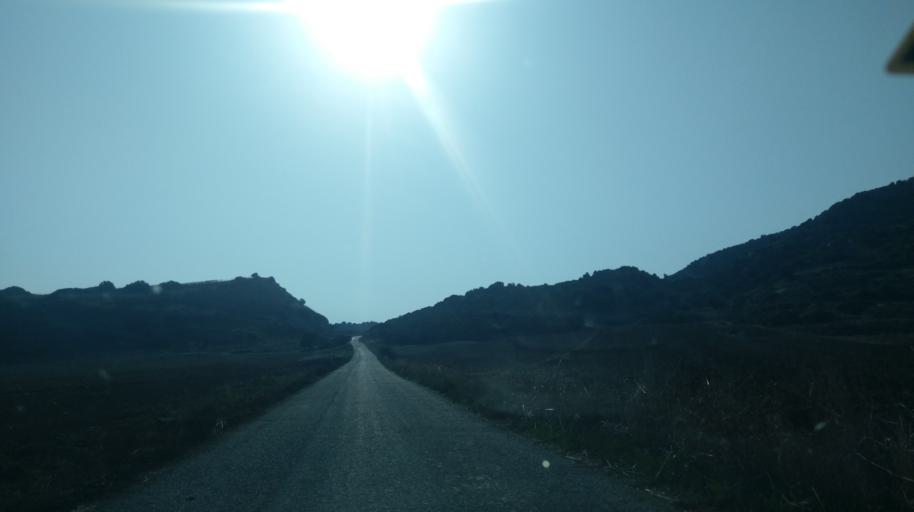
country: CY
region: Ammochostos
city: Rizokarpaso
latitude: 35.5295
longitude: 34.3286
